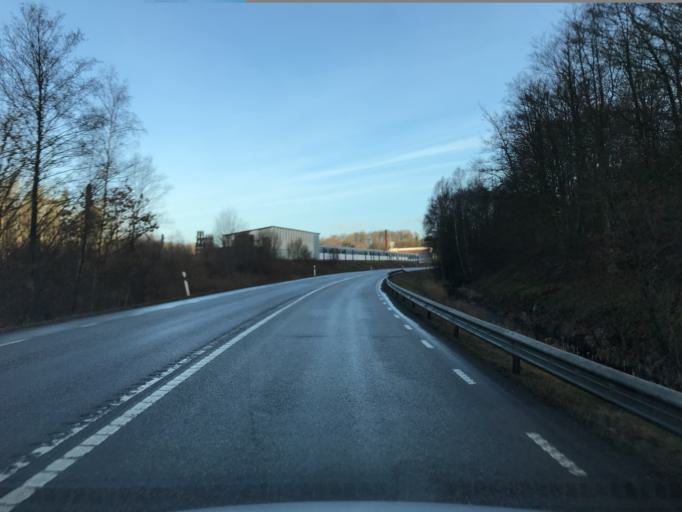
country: SE
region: Skane
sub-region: Hassleholms Kommun
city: Bjarnum
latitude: 56.2744
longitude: 13.7142
